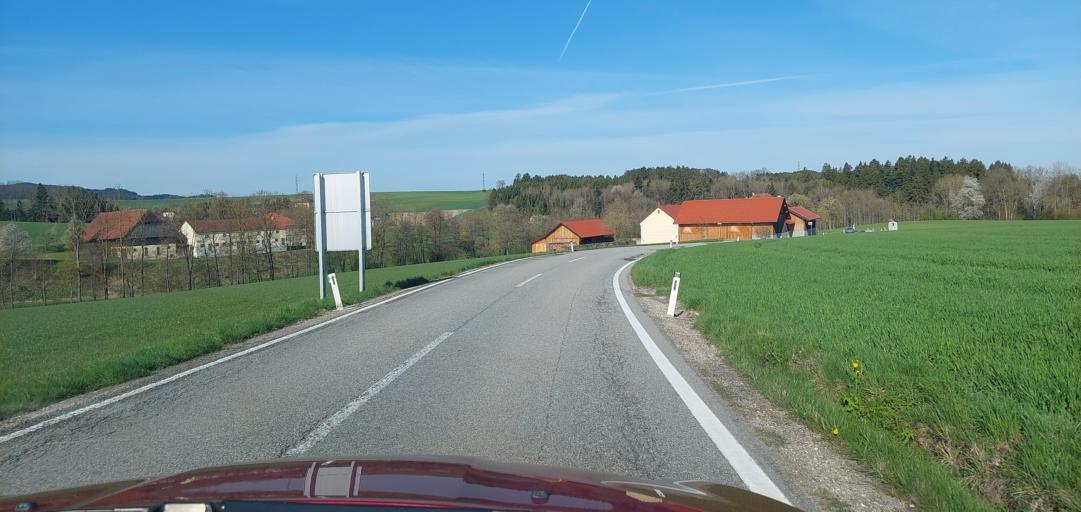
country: AT
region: Upper Austria
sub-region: Politischer Bezirk Ried im Innkreis
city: Ried im Innkreis
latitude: 48.1764
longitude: 13.5503
